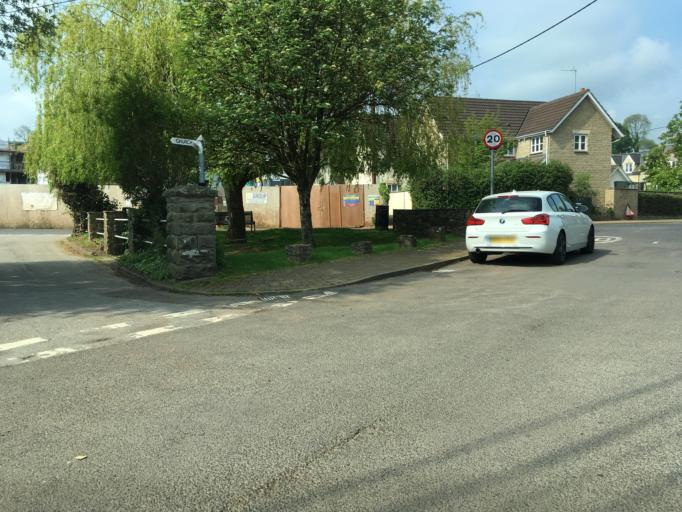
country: GB
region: England
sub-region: North Somerset
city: Winford
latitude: 51.3831
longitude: -2.6620
